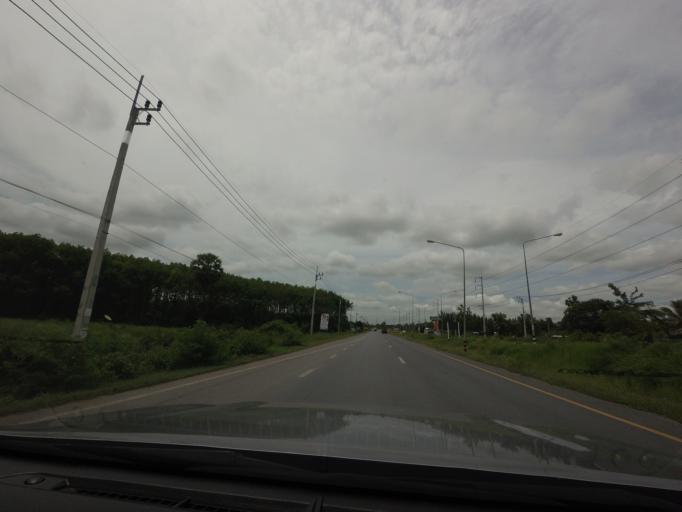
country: TH
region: Nakhon Si Thammarat
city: Hua Sai
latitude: 8.0549
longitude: 100.2091
